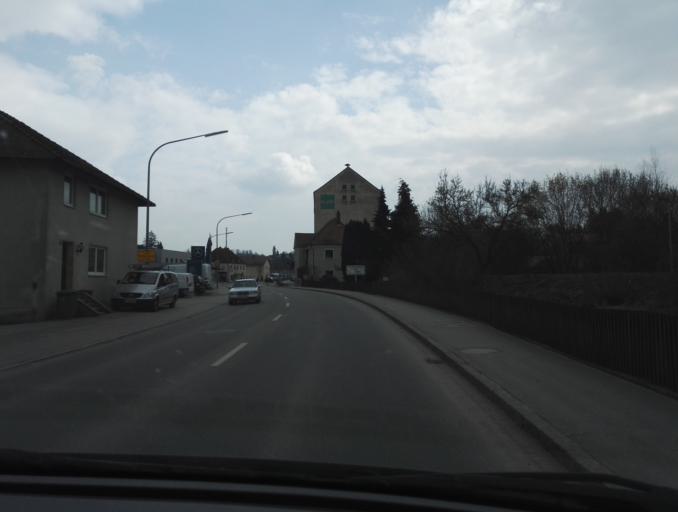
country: DE
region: Bavaria
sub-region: Lower Bavaria
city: Rottenburg an der Laaber
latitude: 48.7084
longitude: 12.0216
